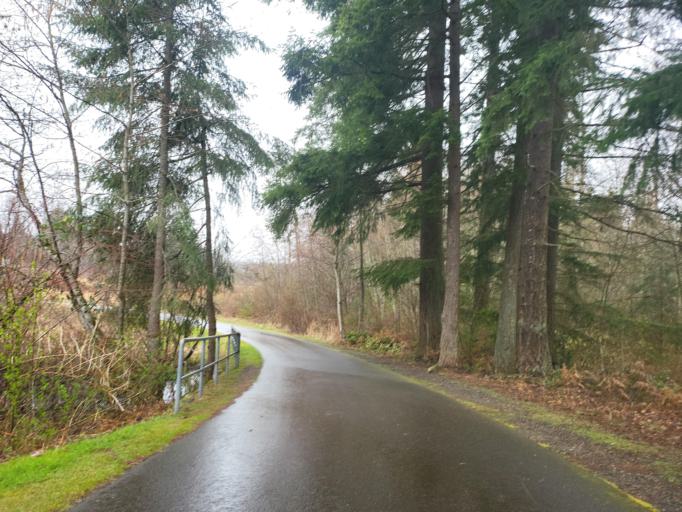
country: US
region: Washington
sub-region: King County
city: East Hill-Meridian
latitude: 47.4241
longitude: -122.1713
